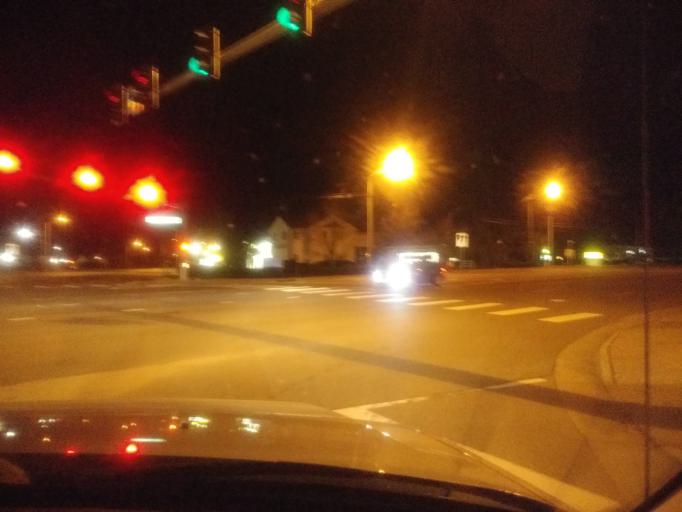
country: US
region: Virginia
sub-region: City of Chesapeake
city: Chesapeake
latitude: 36.7805
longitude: -76.1923
